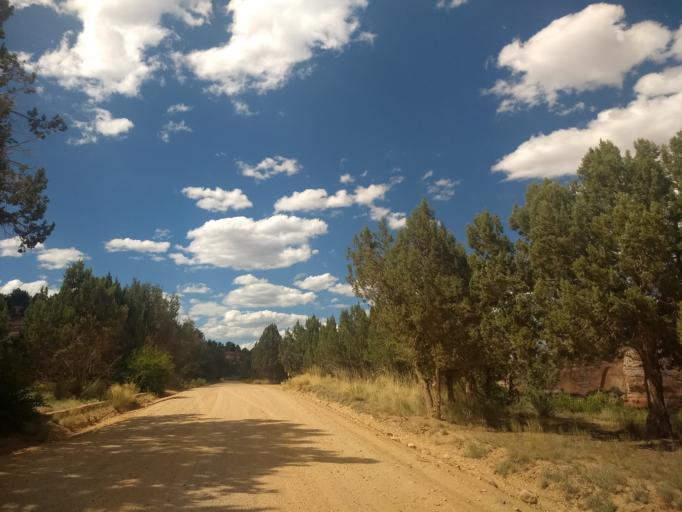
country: US
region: Utah
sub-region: Kane County
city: Kanab
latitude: 37.1475
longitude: -112.5396
